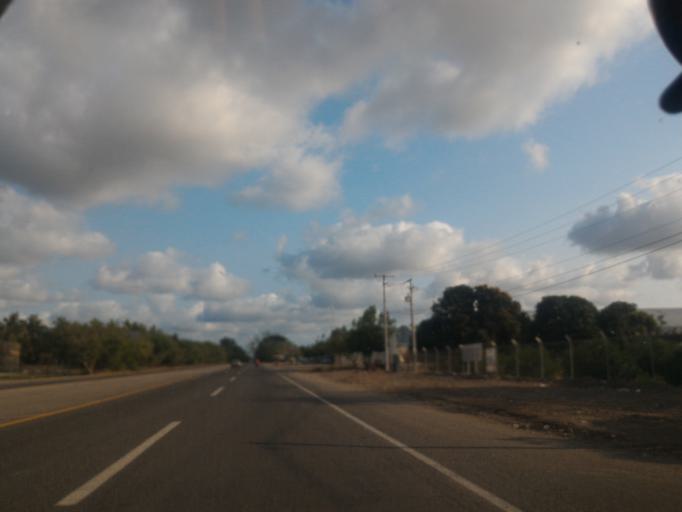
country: MX
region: Colima
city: Tecoman
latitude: 18.8893
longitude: -103.8540
